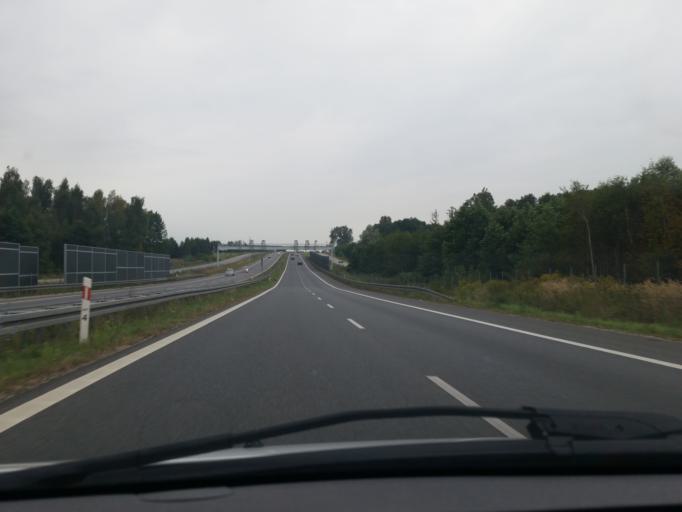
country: PL
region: Masovian Voivodeship
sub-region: Powiat zyrardowski
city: Radziejowice
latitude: 51.9910
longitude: 20.5429
